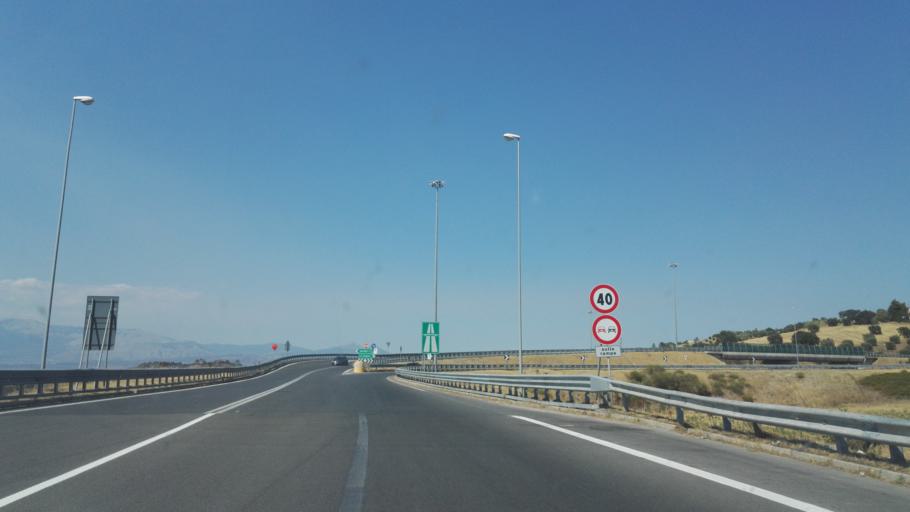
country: IT
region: Calabria
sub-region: Provincia di Cosenza
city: Tarsia
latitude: 39.6262
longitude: 16.2270
